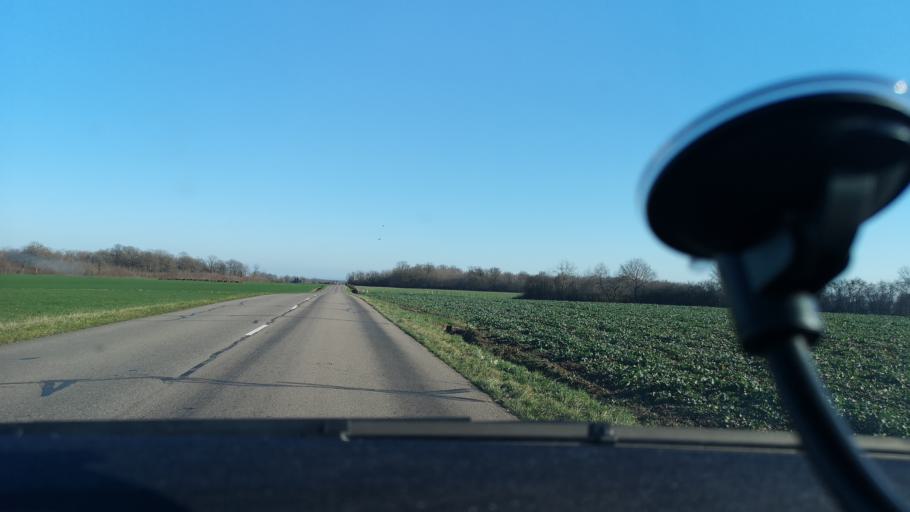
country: FR
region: Bourgogne
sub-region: Departement de Saone-et-Loire
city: Mervans
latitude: 46.7451
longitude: 5.1402
